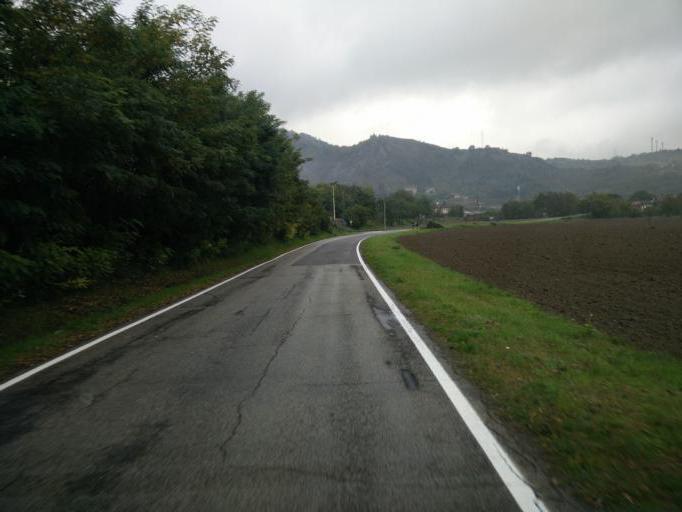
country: IT
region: Emilia-Romagna
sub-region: Provincia di Bologna
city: Marzabotto
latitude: 44.3286
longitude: 11.1871
